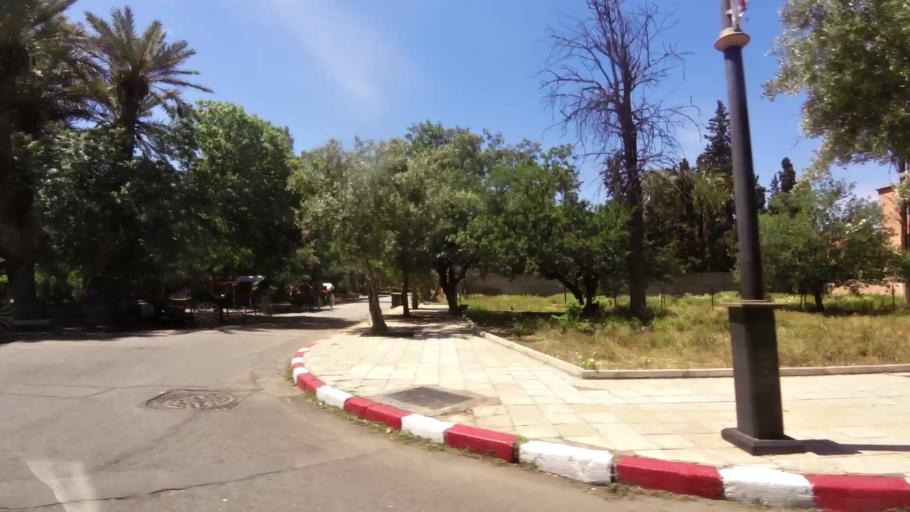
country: MA
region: Marrakech-Tensift-Al Haouz
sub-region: Marrakech
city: Marrakesh
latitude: 31.6233
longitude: -8.0082
